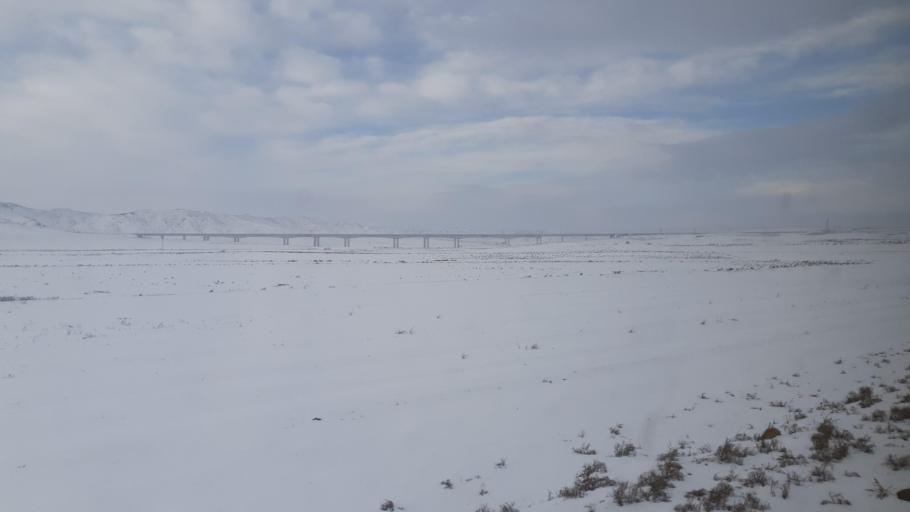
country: TR
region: Kirikkale
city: Delice
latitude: 39.8938
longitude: 33.9897
